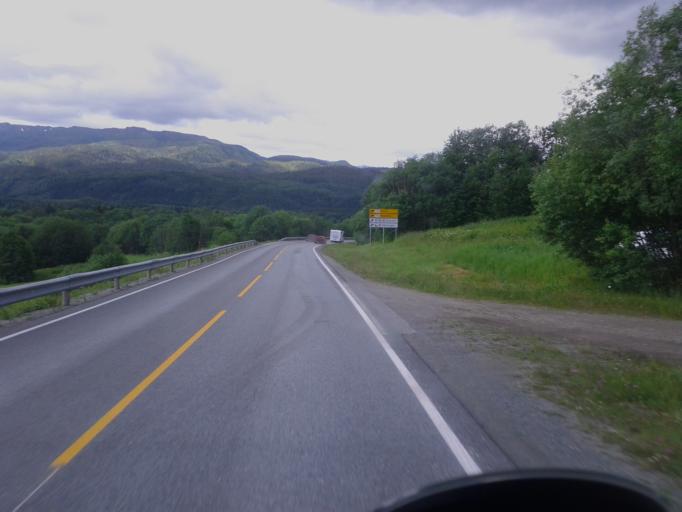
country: NO
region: Nord-Trondelag
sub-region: Grong
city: Grong
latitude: 64.5334
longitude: 12.4103
